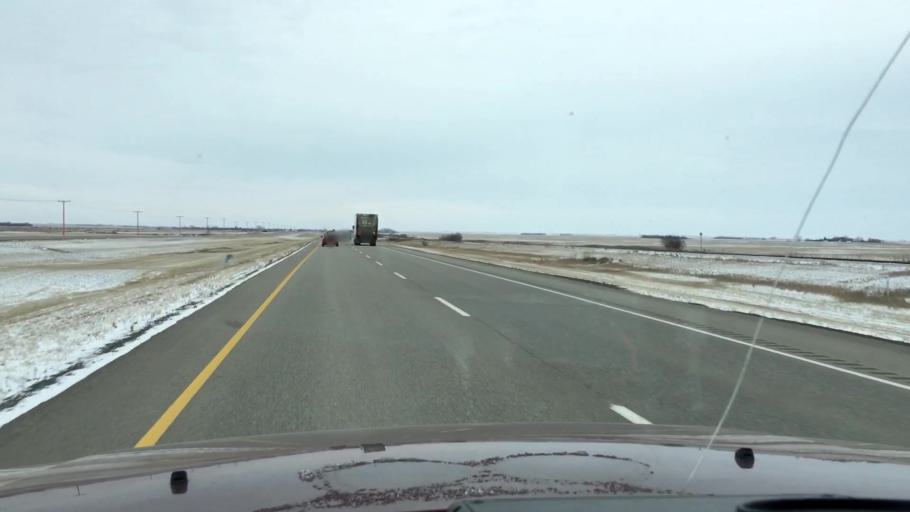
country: CA
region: Saskatchewan
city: Watrous
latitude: 51.1873
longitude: -105.9455
